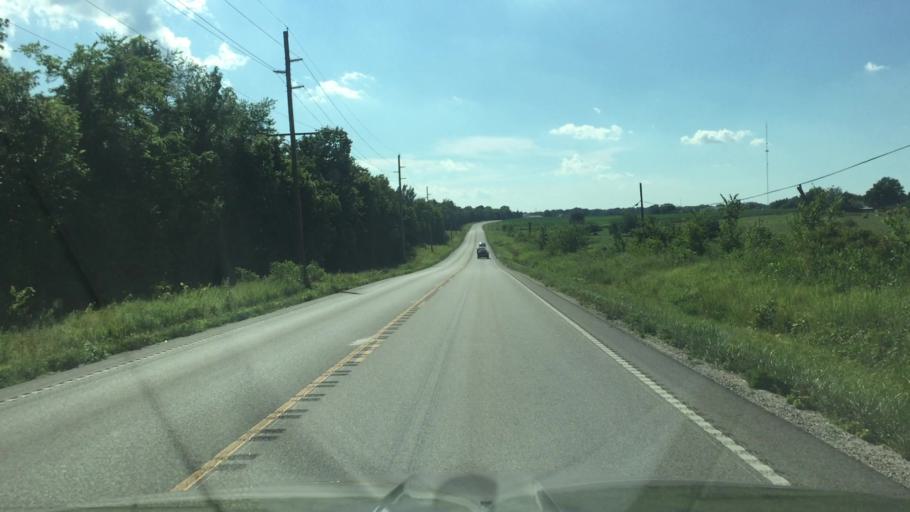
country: US
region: Missouri
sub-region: Morgan County
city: Versailles
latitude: 38.4030
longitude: -92.7506
